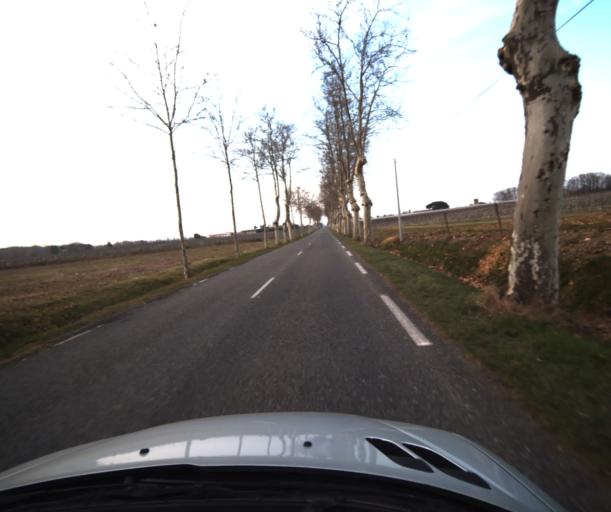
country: FR
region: Midi-Pyrenees
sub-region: Departement du Tarn-et-Garonne
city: Labastide-Saint-Pierre
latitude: 43.8804
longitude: 1.3771
